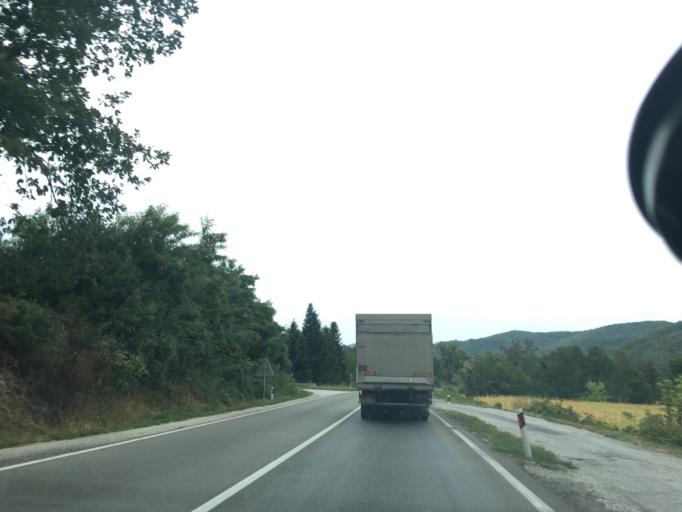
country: RS
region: Central Serbia
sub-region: Moravicki Okrug
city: Cacak
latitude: 43.9007
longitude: 20.2618
